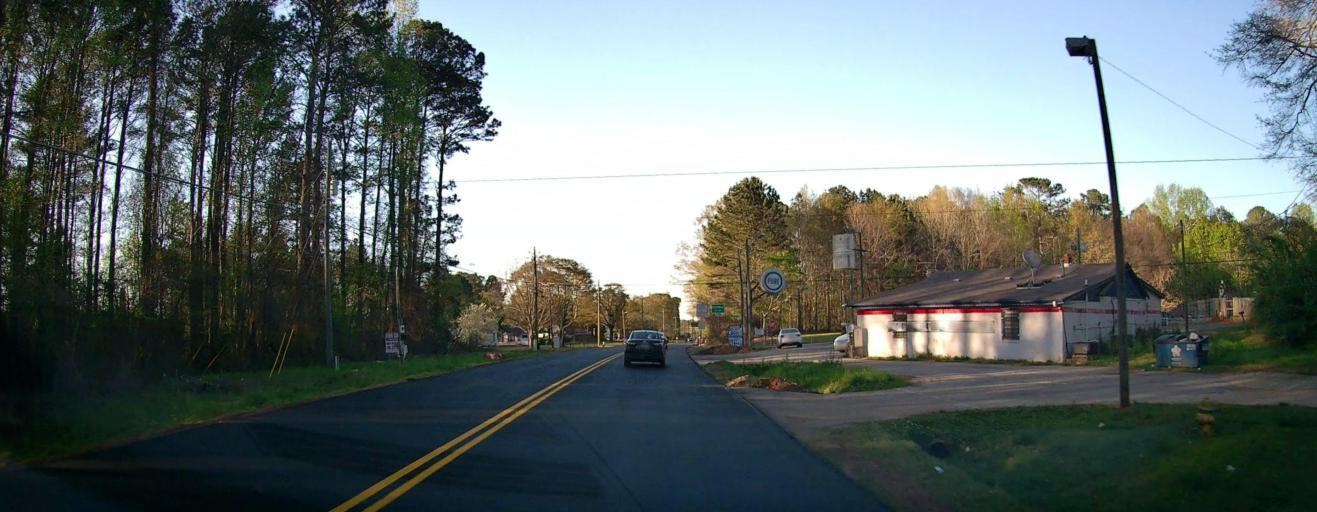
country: US
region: Georgia
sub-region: Newton County
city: Porterdale
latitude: 33.5582
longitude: -83.9061
